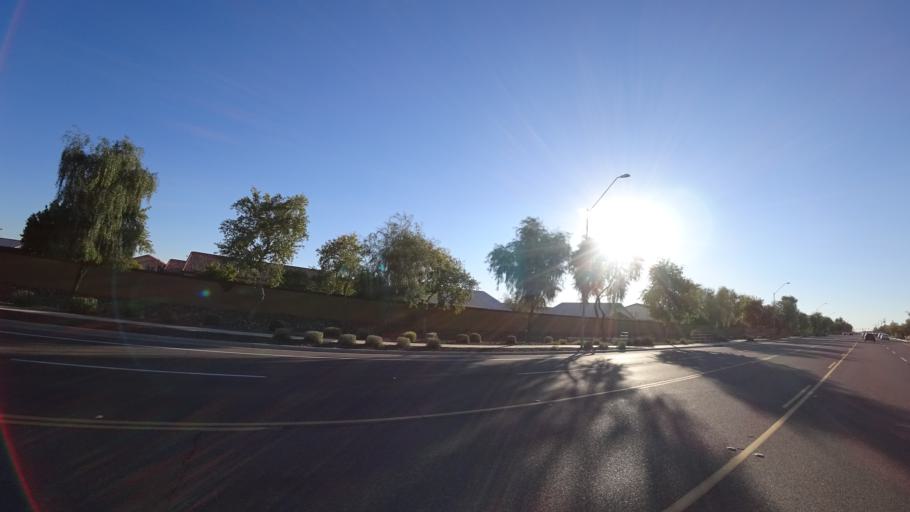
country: US
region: Arizona
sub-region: Maricopa County
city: Sun City
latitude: 33.6817
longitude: -112.2474
